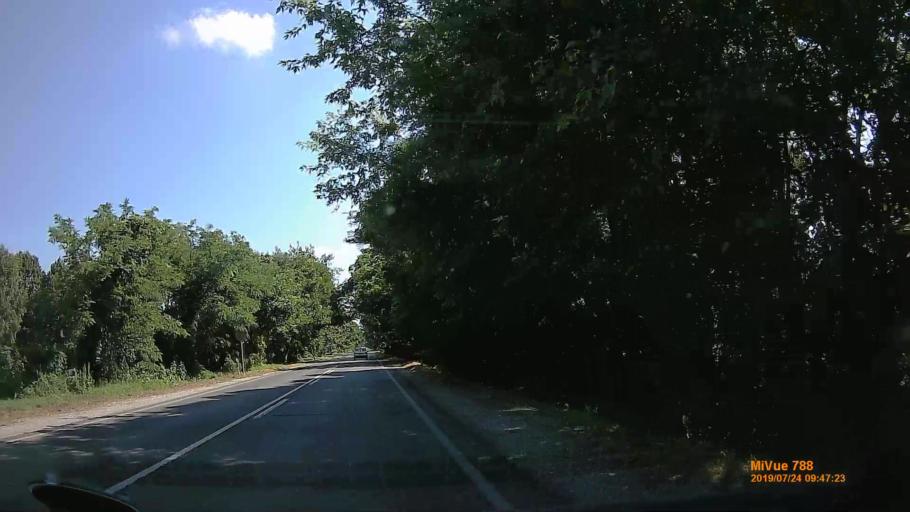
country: HU
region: Szabolcs-Szatmar-Bereg
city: Baktaloranthaza
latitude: 47.9961
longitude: 22.0980
